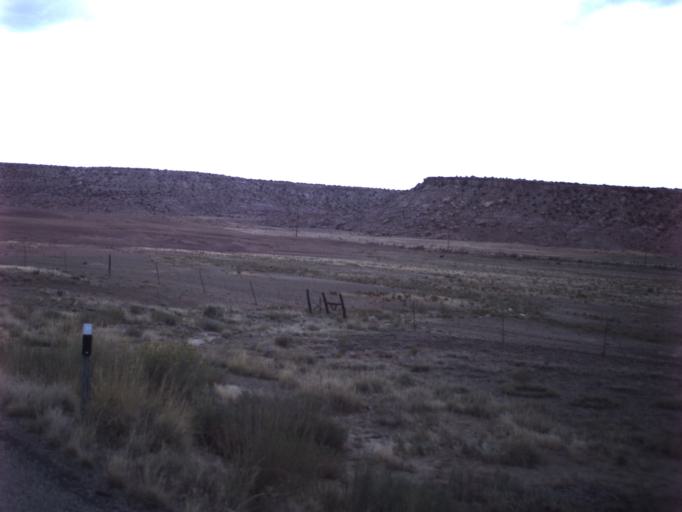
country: US
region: Utah
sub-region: San Juan County
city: Blanding
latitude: 37.4293
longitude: -109.4094
